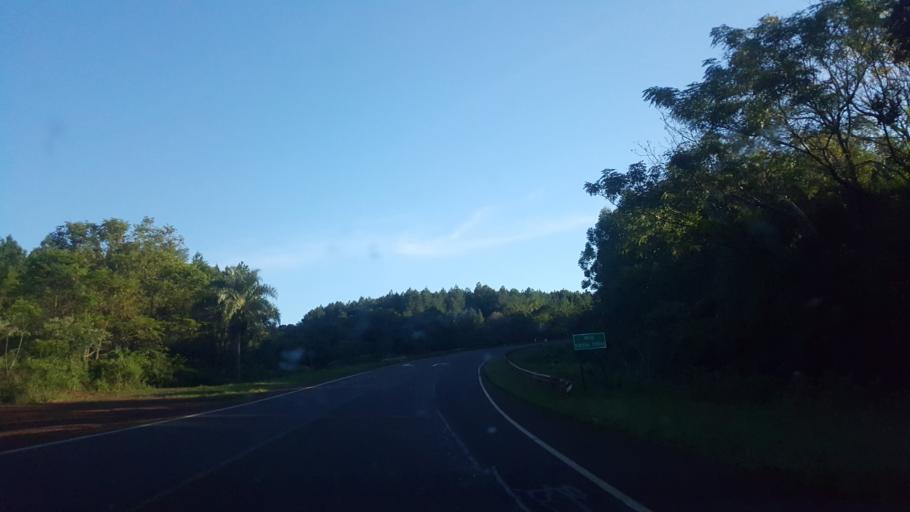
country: AR
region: Misiones
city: Caraguatay
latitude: -26.6614
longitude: -54.7535
